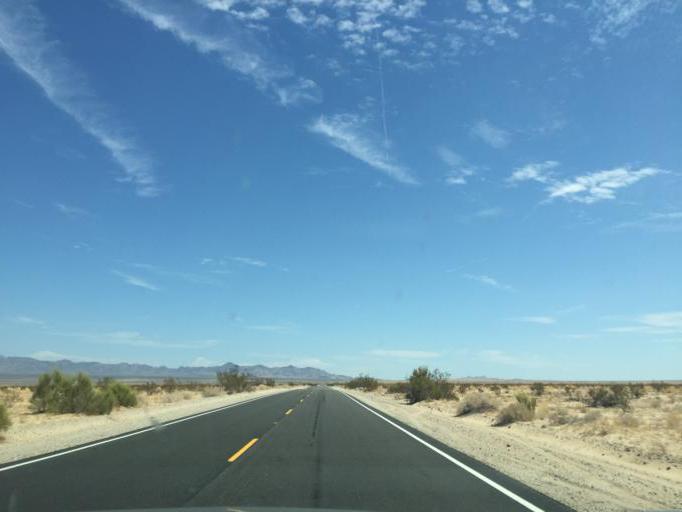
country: US
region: California
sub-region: Riverside County
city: Mesa Verde
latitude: 34.0973
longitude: -115.0255
